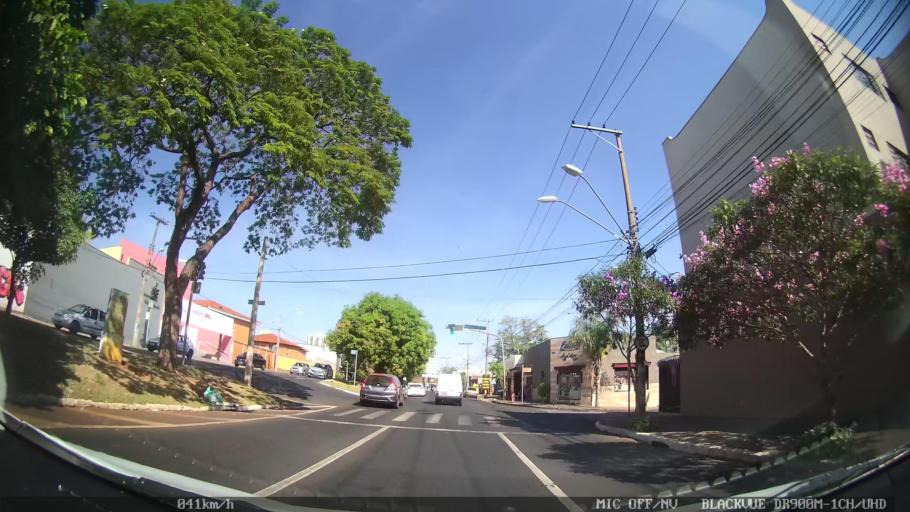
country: BR
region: Sao Paulo
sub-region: Ribeirao Preto
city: Ribeirao Preto
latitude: -21.1858
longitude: -47.8196
